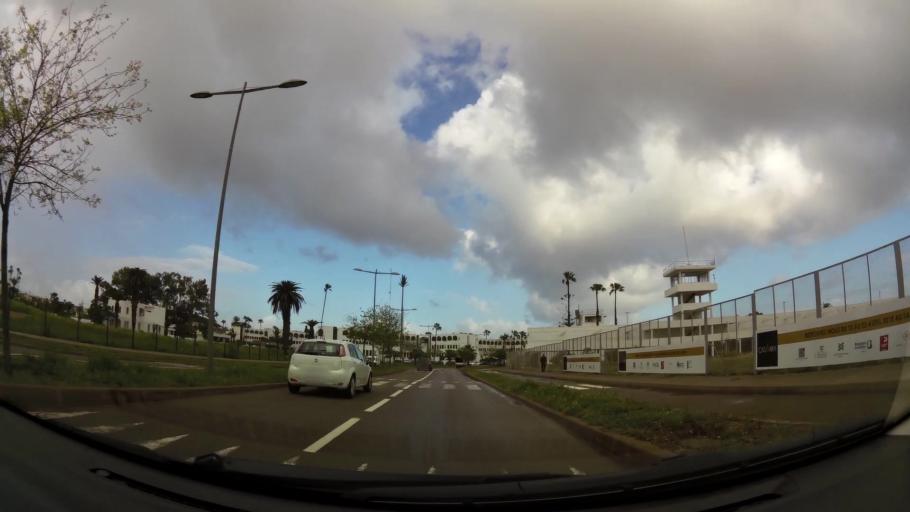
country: MA
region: Grand Casablanca
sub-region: Casablanca
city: Casablanca
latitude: 33.5620
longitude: -7.6623
